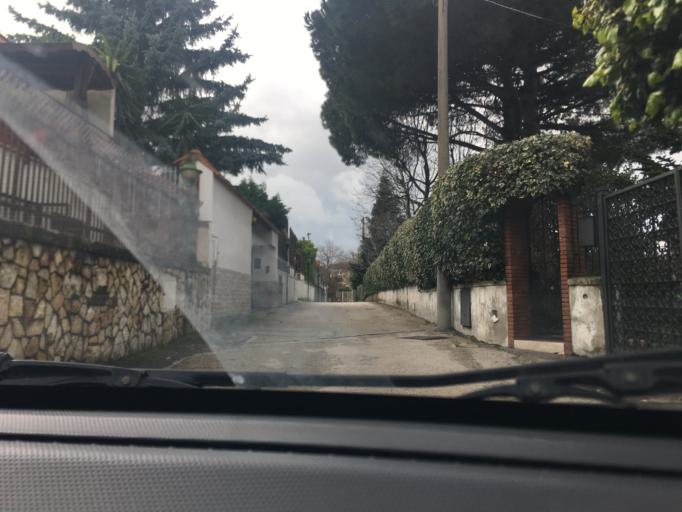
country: IT
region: Campania
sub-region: Provincia di Napoli
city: Marano di Napoli
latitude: 40.8915
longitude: 14.1790
